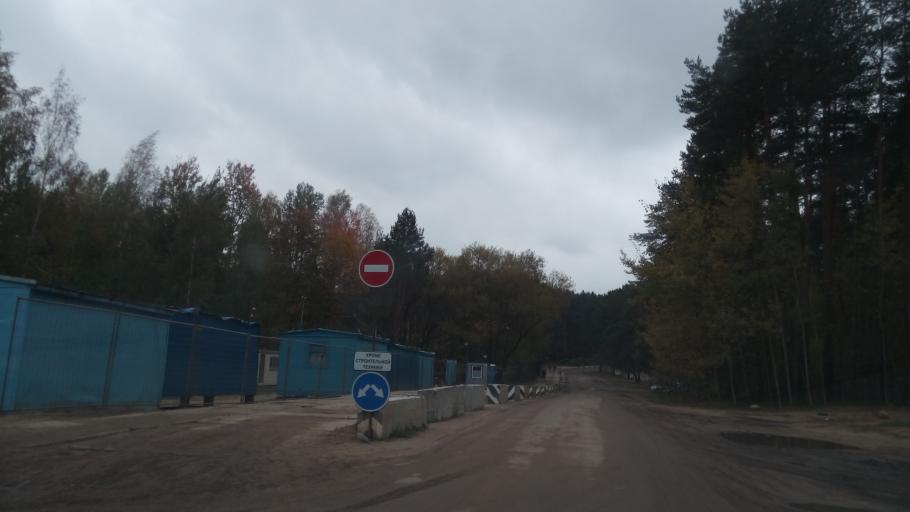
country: BY
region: Minsk
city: Zhdanovichy
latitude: 53.9580
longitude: 27.4421
